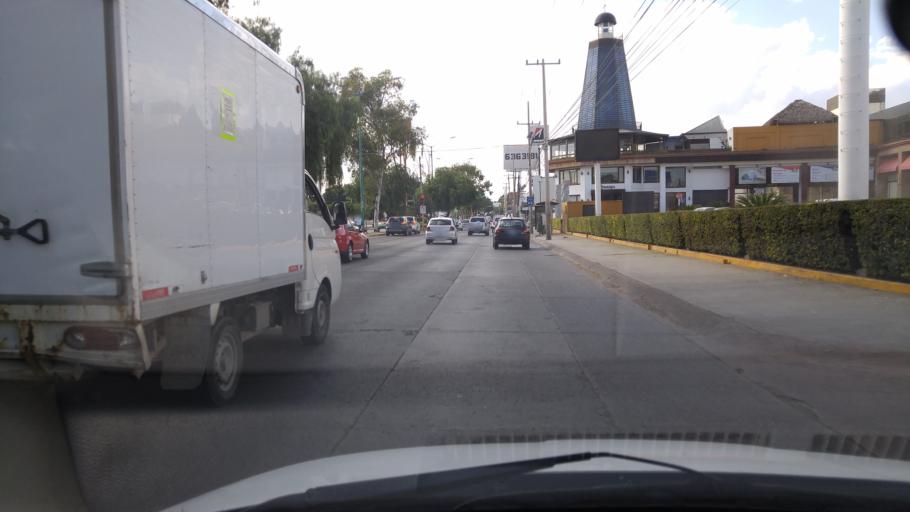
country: MX
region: Guanajuato
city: Leon
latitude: 21.1073
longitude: -101.6596
